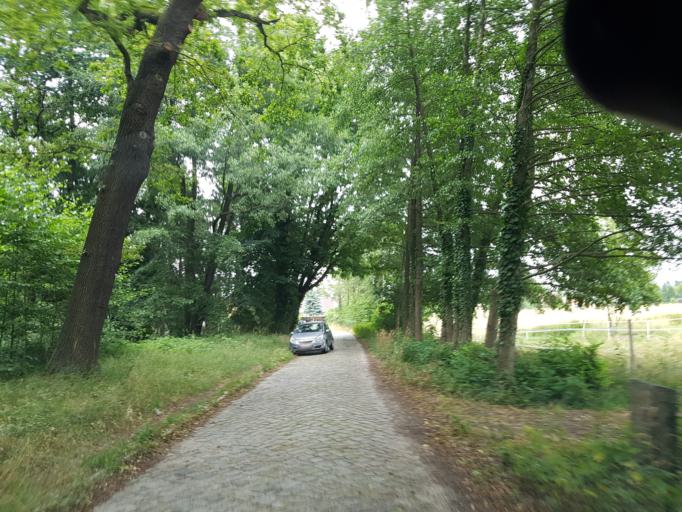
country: DE
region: Brandenburg
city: Sallgast
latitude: 51.5852
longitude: 13.8456
